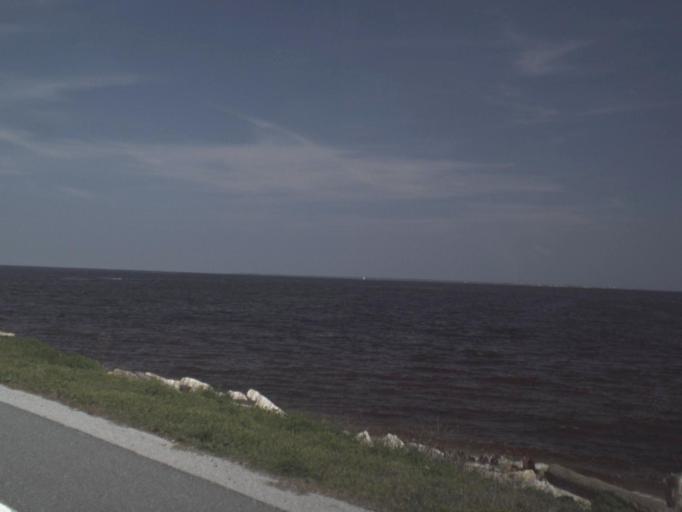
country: US
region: Florida
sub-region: Franklin County
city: Carrabelle
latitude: 29.8161
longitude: -84.7143
